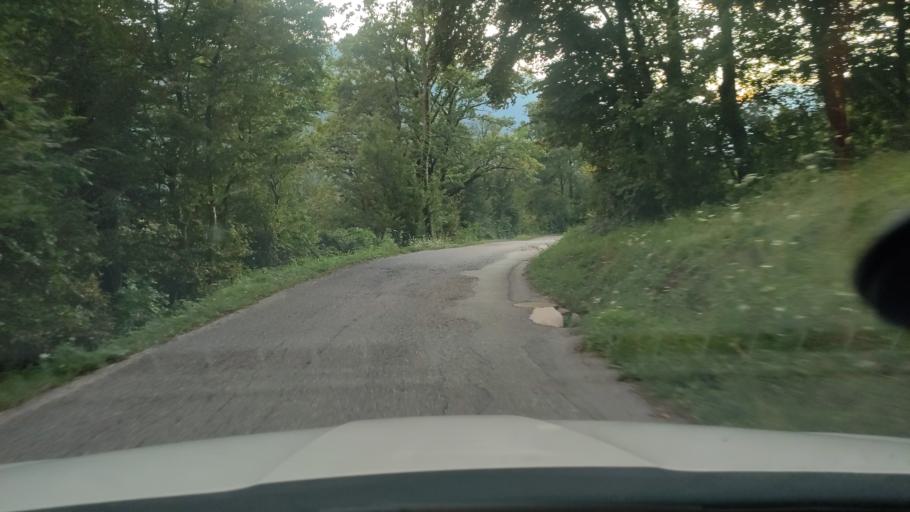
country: IT
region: Friuli Venezia Giulia
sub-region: Provincia di Udine
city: Cras
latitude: 46.2161
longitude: 13.6390
